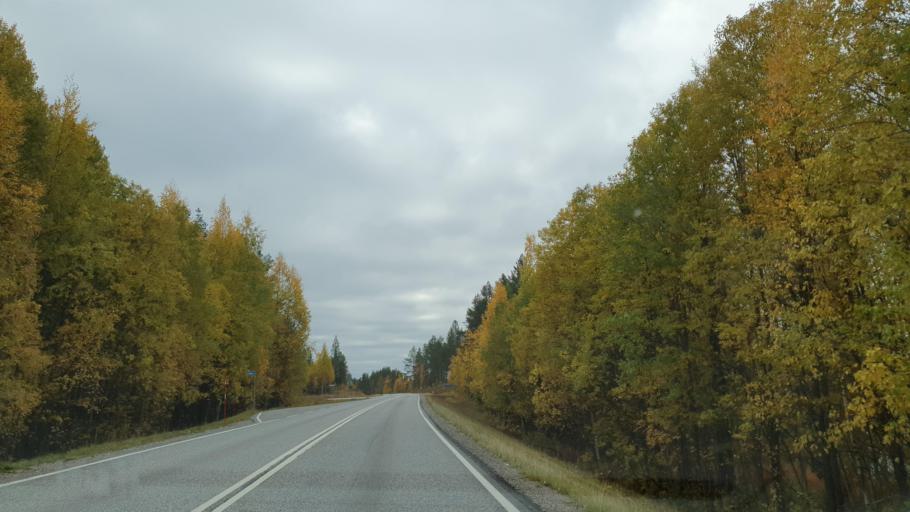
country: FI
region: Lapland
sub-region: Rovaniemi
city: Ranua
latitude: 66.1986
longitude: 26.2237
